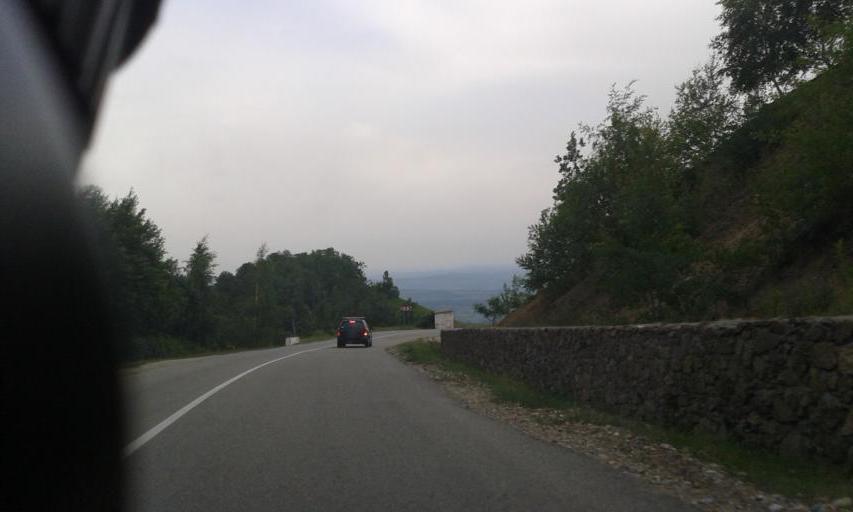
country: RO
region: Gorj
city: Novaci-Straini
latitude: 45.2261
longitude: 23.6949
